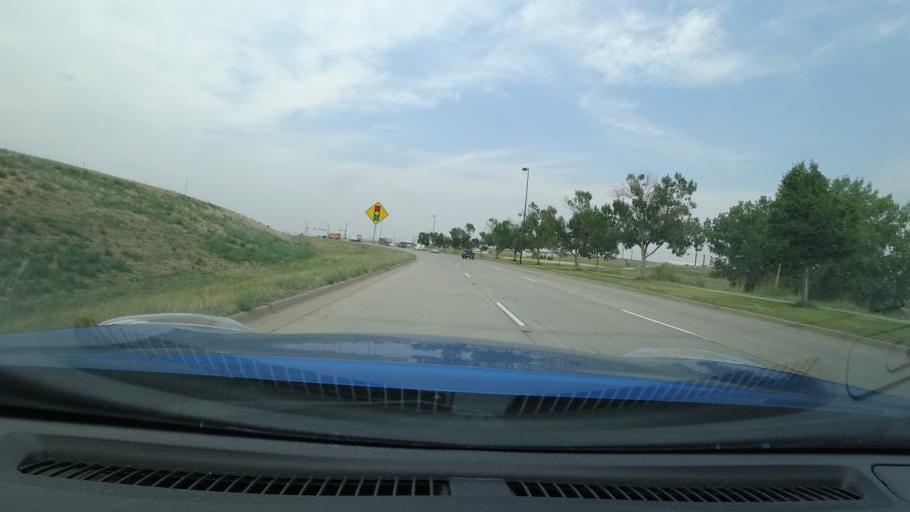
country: US
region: Colorado
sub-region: Adams County
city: Aurora
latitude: 39.7702
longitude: -104.7904
